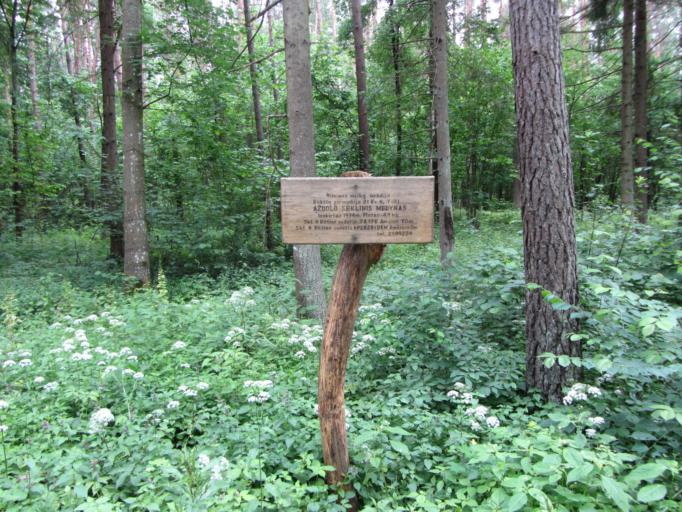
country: LT
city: Grigiskes
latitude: 54.8011
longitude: 24.9845
